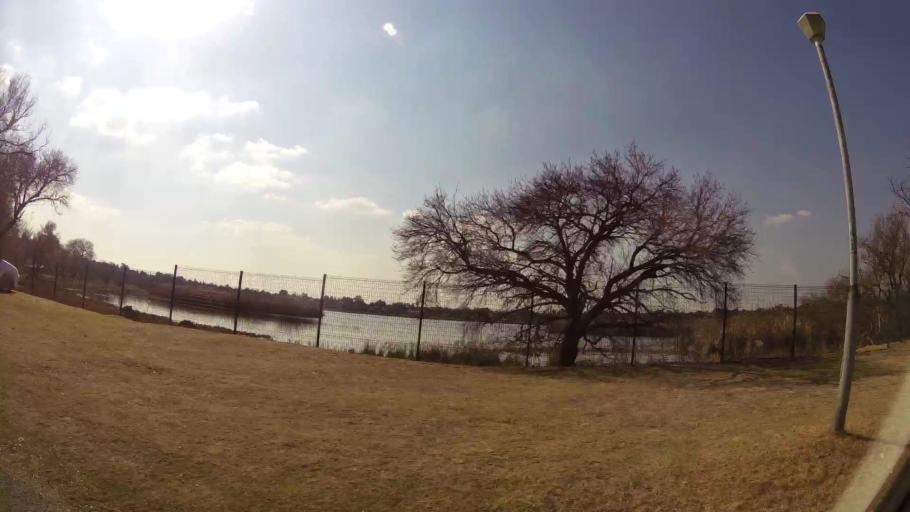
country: ZA
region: Gauteng
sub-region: Ekurhuleni Metropolitan Municipality
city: Benoni
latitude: -26.1953
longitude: 28.2911
